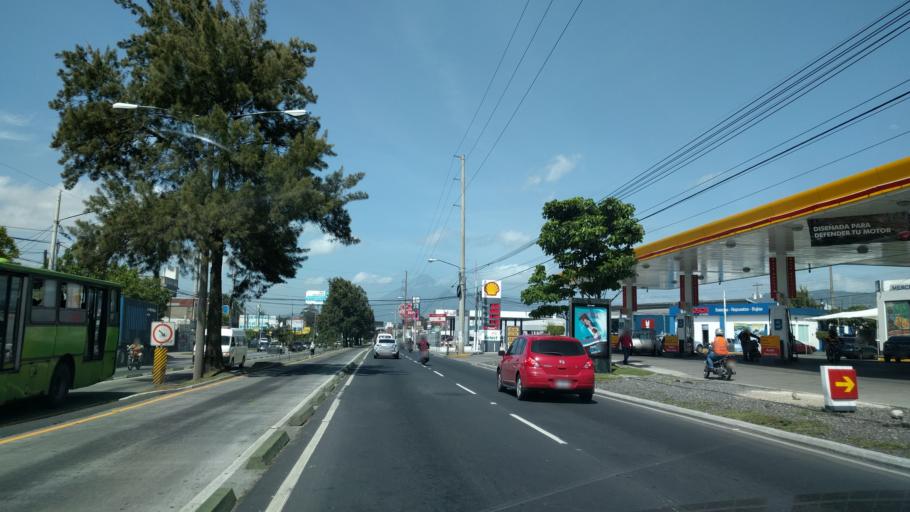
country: GT
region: Guatemala
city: Guatemala City
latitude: 14.6008
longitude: -90.5502
